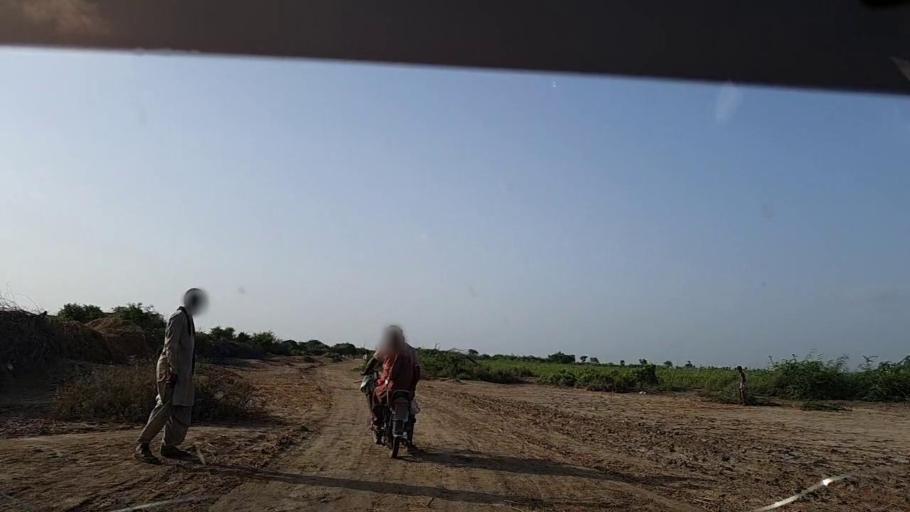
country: PK
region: Sindh
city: Badin
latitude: 24.5725
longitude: 68.8764
